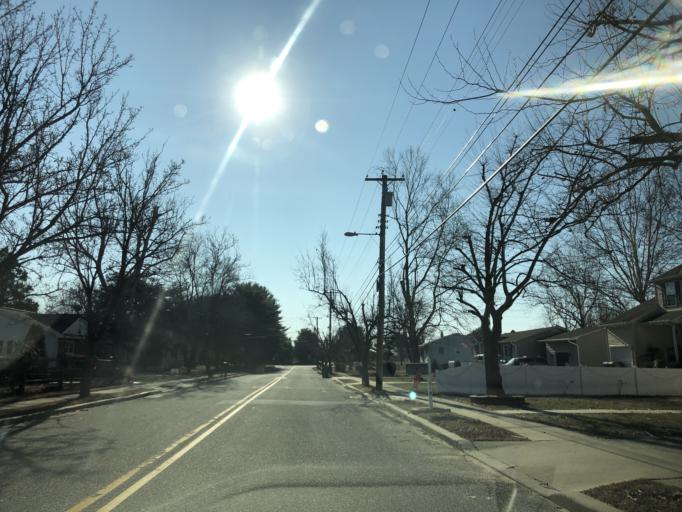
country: US
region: Pennsylvania
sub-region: Delaware County
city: Chester
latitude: 39.8020
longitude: -75.3399
